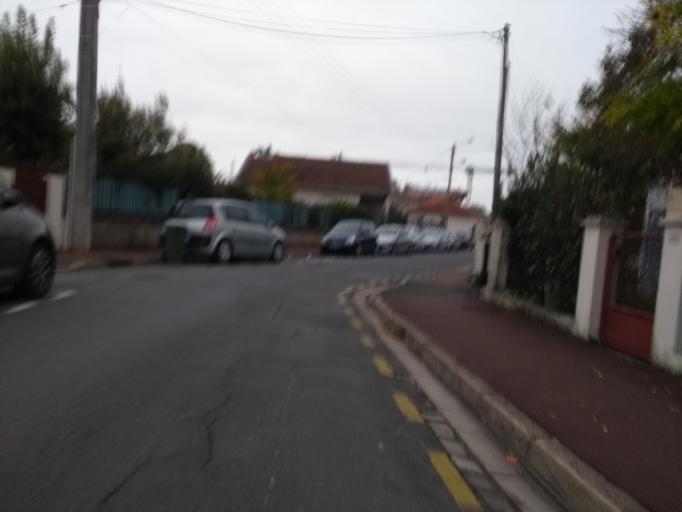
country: FR
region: Aquitaine
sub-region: Departement de la Gironde
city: Talence
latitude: 44.8035
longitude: -0.5983
